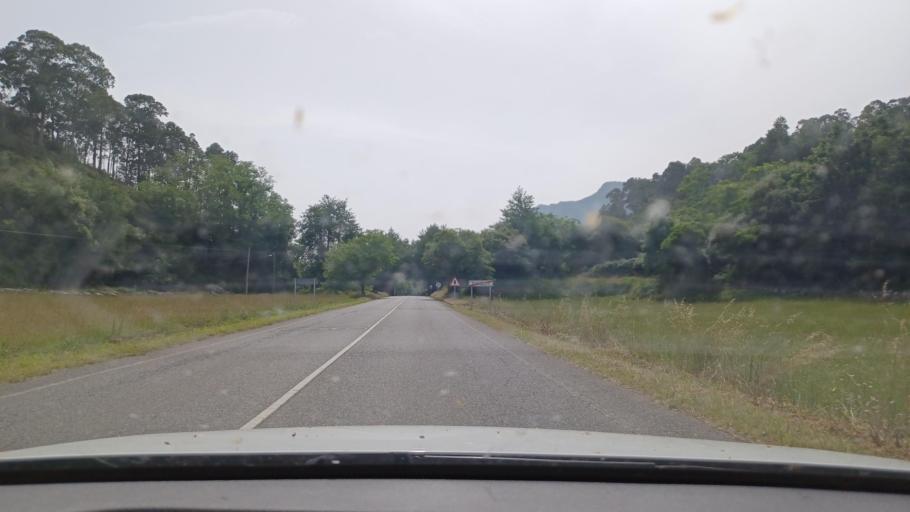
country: ES
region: Asturias
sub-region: Province of Asturias
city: Ribadesella
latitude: 43.4442
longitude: -5.0038
